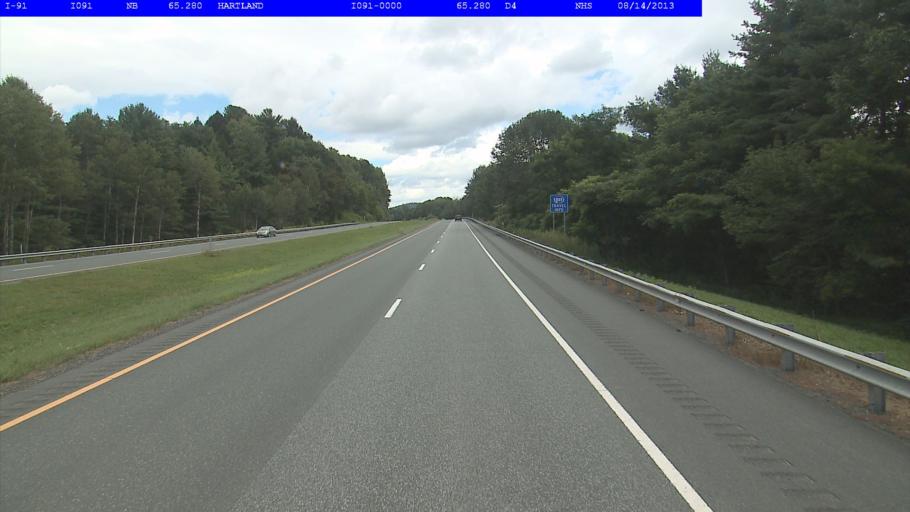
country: US
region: Vermont
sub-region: Windsor County
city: White River Junction
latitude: 43.5869
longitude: -72.3681
